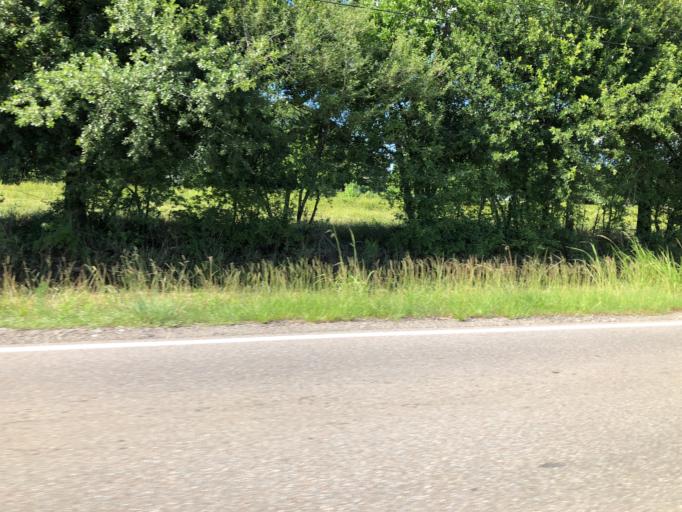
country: US
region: Texas
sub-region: Harris County
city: Katy
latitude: 29.8314
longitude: -95.8060
